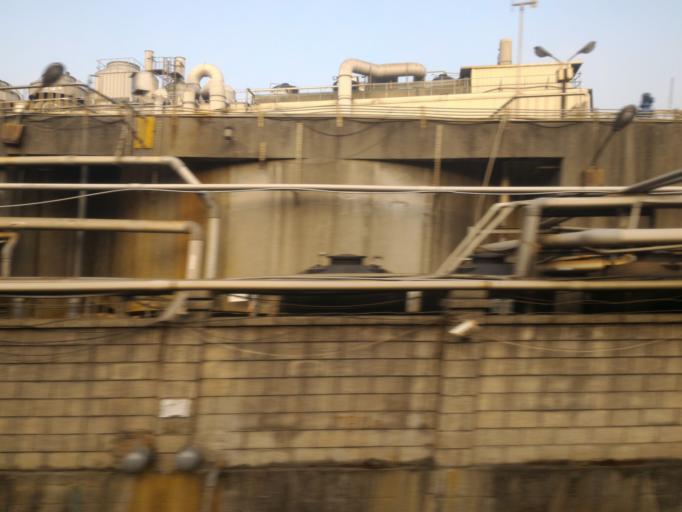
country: TW
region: Taiwan
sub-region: Taoyuan
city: Taoyuan
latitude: 24.9809
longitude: 121.3288
